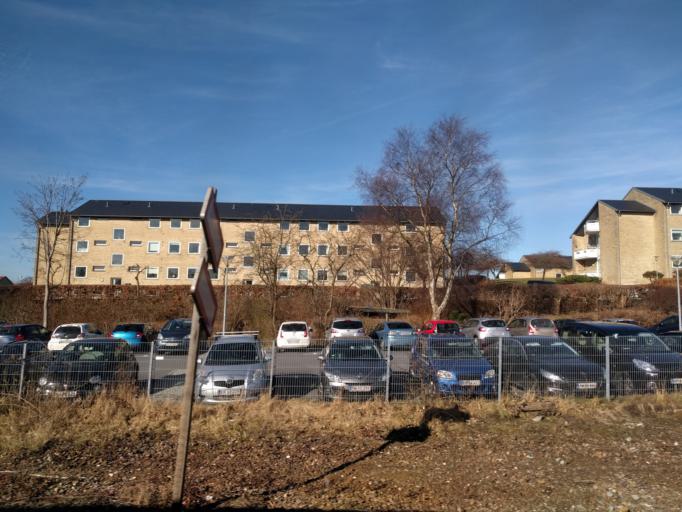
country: DK
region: Capital Region
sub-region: Helsingor Kommune
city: Espergaerde
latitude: 55.9911
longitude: 12.5476
